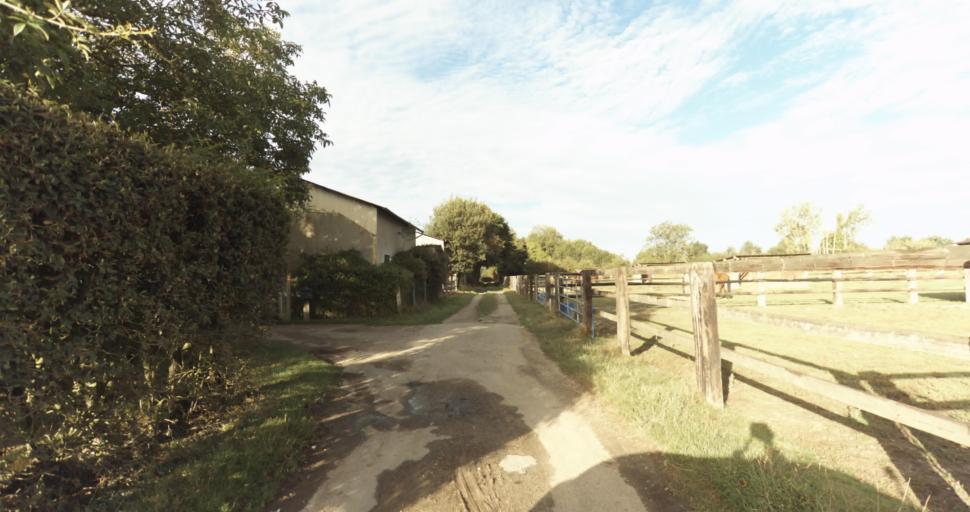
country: FR
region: Lower Normandy
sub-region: Departement de l'Orne
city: Vimoutiers
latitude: 48.8776
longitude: 0.2486
